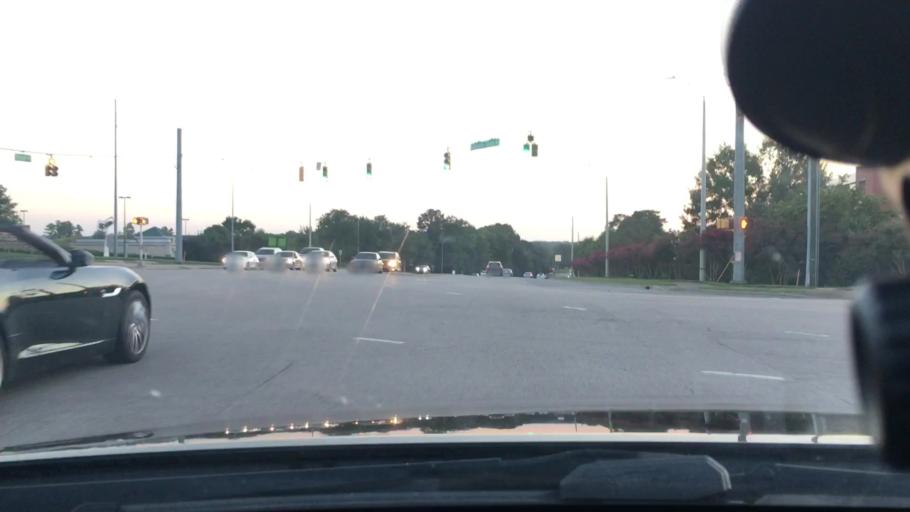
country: US
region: North Carolina
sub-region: Wake County
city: Cary
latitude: 35.7400
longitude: -78.7797
